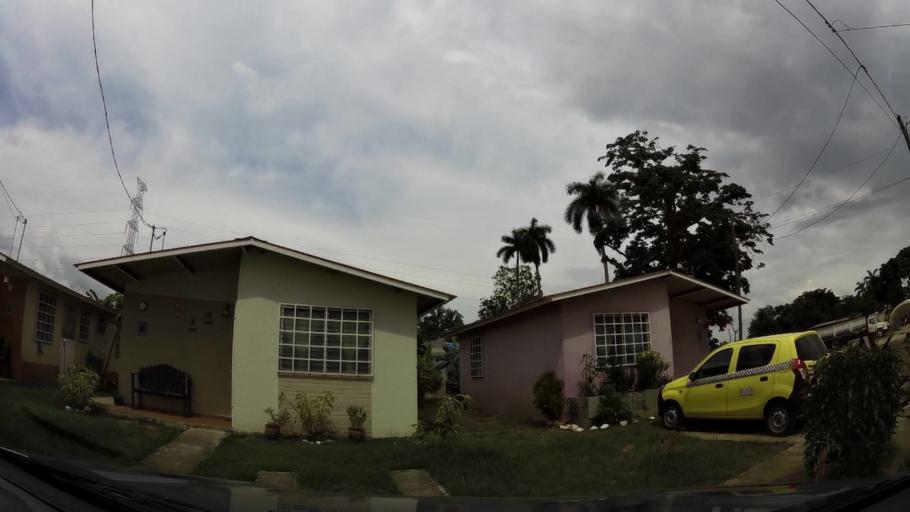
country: PA
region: Panama
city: Los Lotes
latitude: 9.1119
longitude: -79.3113
